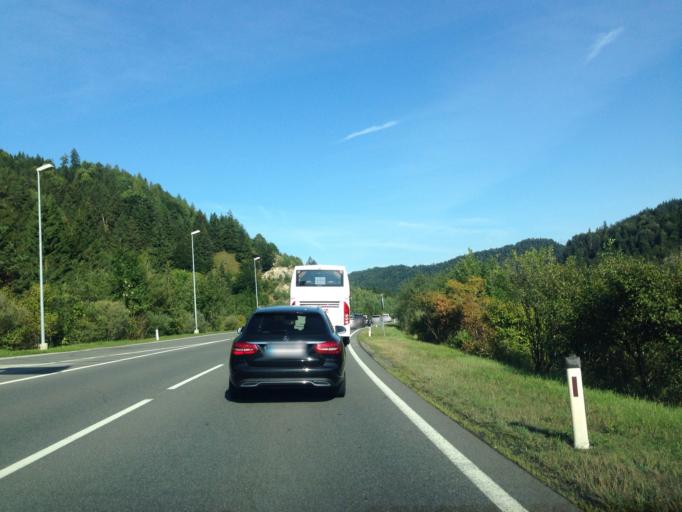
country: AT
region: Tyrol
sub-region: Politischer Bezirk Reutte
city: Musau
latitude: 47.5402
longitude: 10.6669
